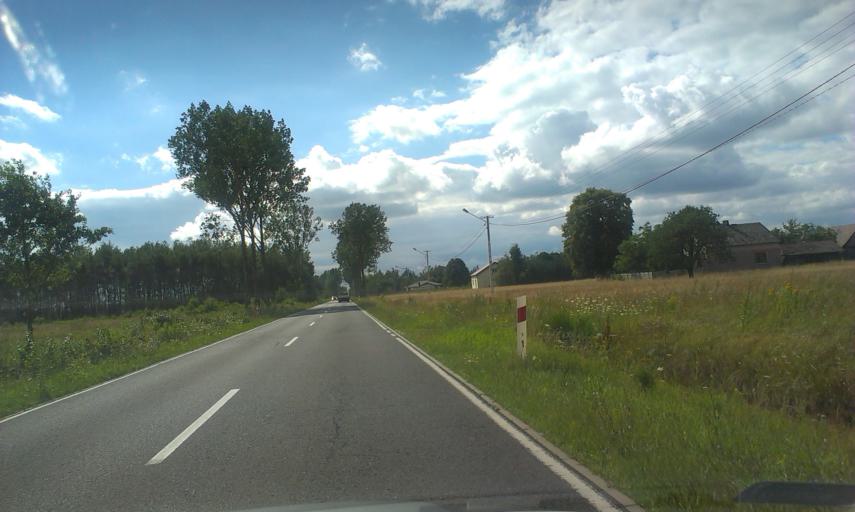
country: PL
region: Lodz Voivodeship
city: Zabia Wola
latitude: 51.9664
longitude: 20.6651
